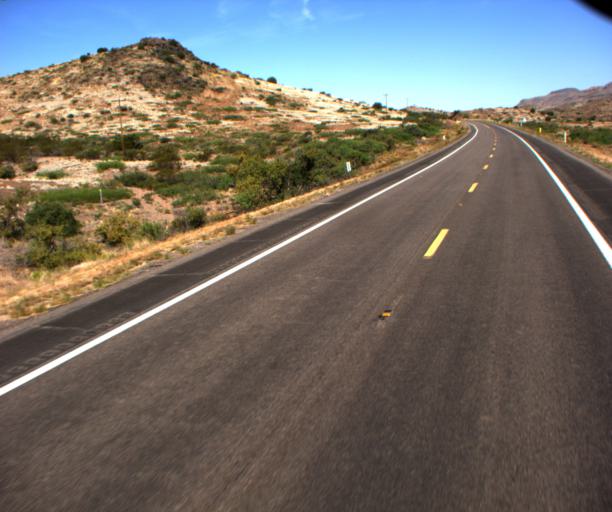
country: US
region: Arizona
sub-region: Greenlee County
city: Clifton
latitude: 32.7677
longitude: -109.2564
